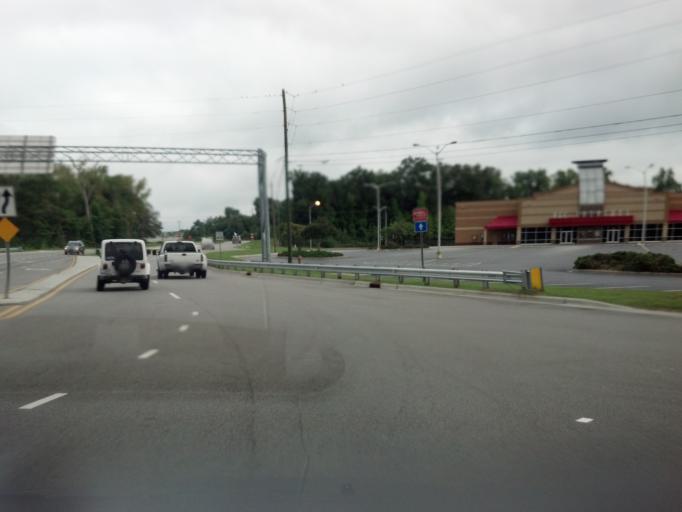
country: US
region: North Carolina
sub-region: Nash County
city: Rocky Mount
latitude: 35.9659
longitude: -77.8042
